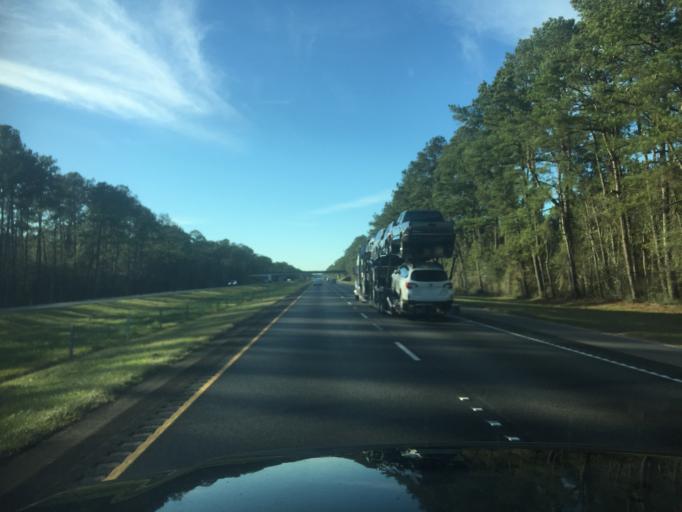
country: US
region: Louisiana
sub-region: Saint Tammany Parish
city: Slidell
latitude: 30.3229
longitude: -89.8528
